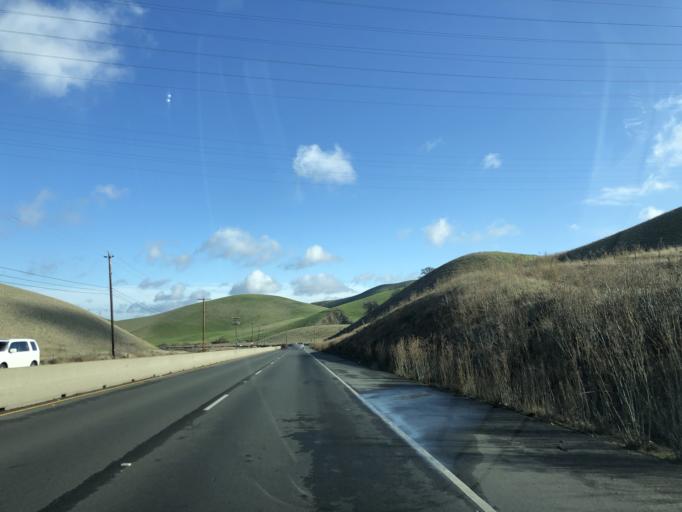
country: US
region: California
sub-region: Contra Costa County
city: Clayton
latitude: 37.9775
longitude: -121.9051
